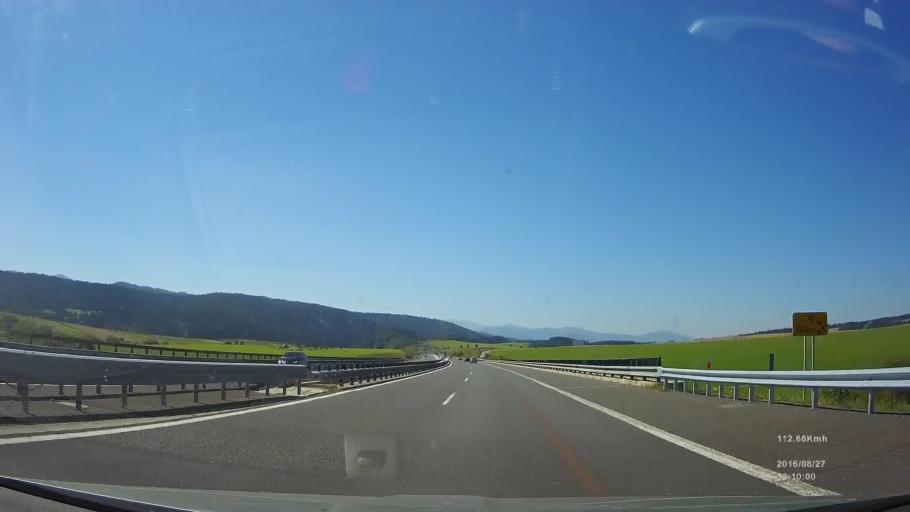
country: SK
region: Presovsky
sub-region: Okres Poprad
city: Strba
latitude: 49.0698
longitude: 19.9761
